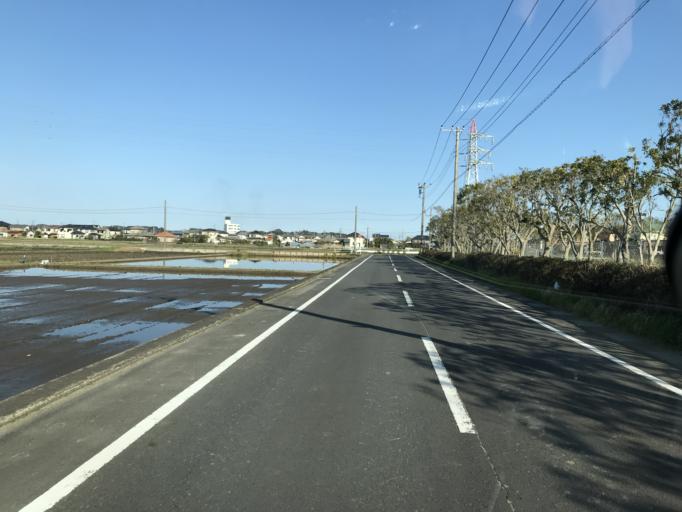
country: JP
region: Chiba
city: Omigawa
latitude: 35.8467
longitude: 140.6121
